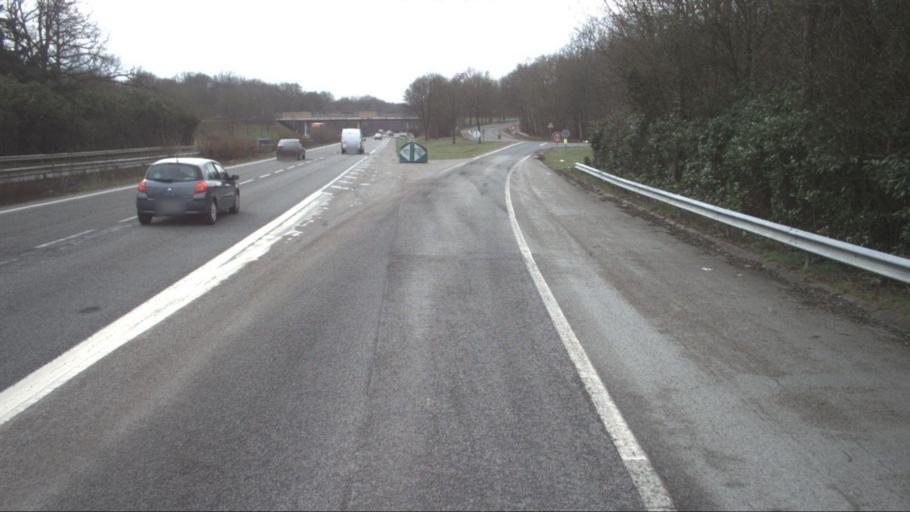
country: FR
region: Ile-de-France
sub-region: Departement des Yvelines
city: Le Perray-en-Yvelines
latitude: 48.6827
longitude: 1.8413
